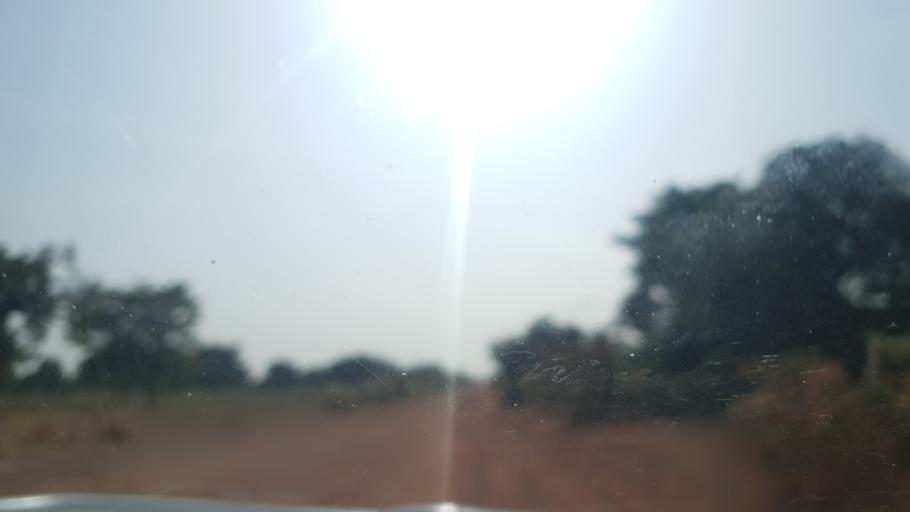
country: ML
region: Koulikoro
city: Dioila
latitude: 12.7033
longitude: -6.7665
